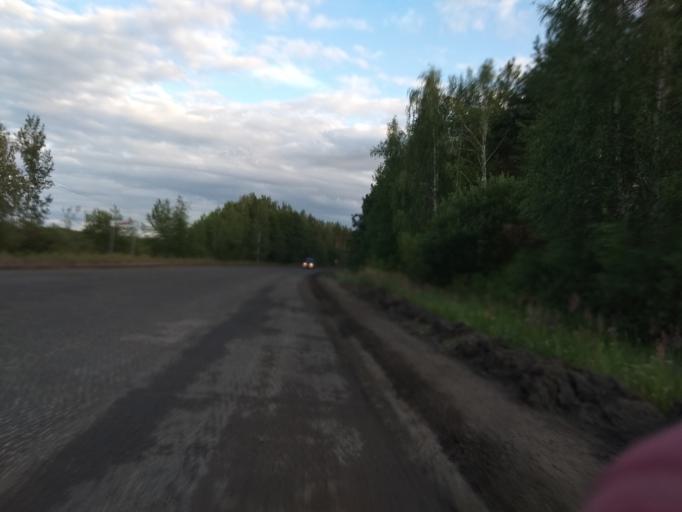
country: RU
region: Moskovskaya
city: Misheronskiy
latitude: 55.6480
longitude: 39.7571
